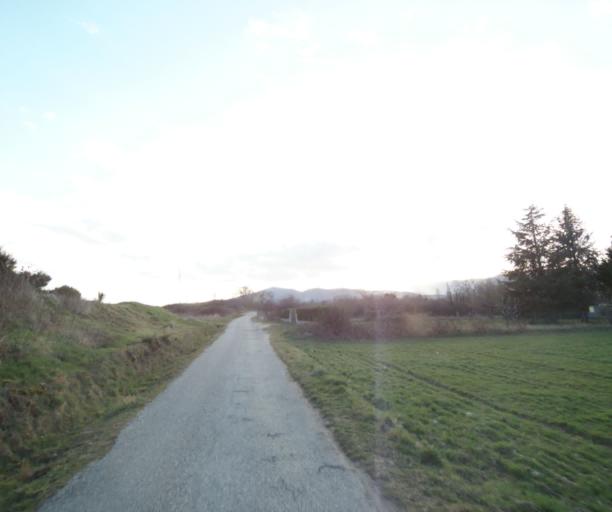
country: FR
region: Rhone-Alpes
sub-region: Departement de l'Ardeche
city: Davezieux
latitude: 45.2437
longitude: 4.7032
